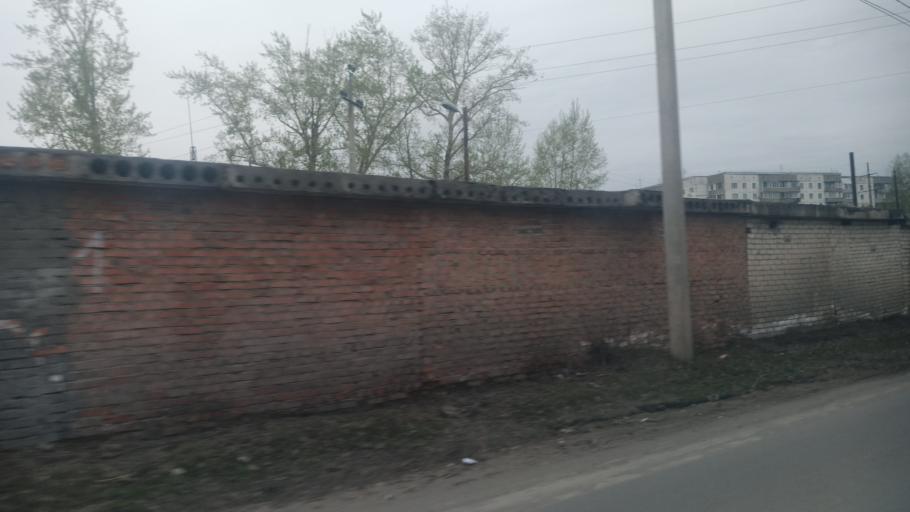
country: RU
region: Altai Krai
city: Yuzhnyy
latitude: 53.2491
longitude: 83.6913
